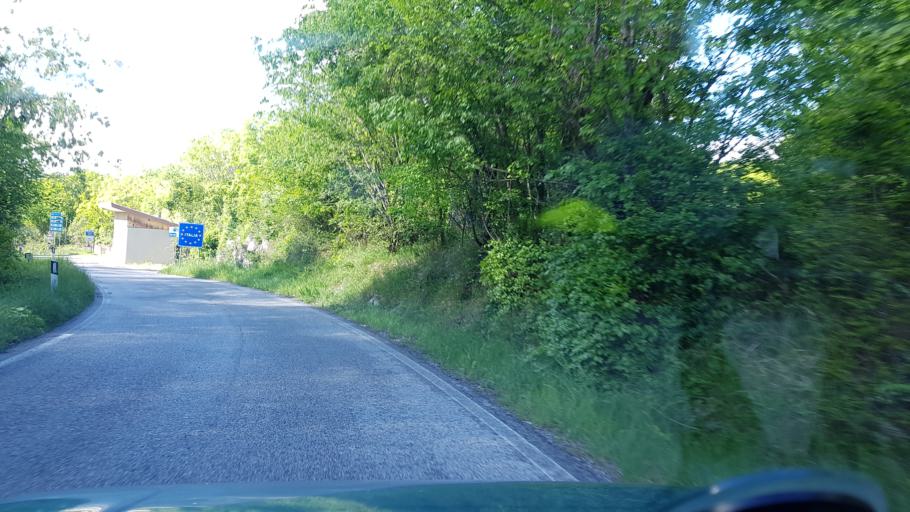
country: SI
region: Miren-Kostanjevica
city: Miren
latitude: 45.8674
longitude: 13.5847
